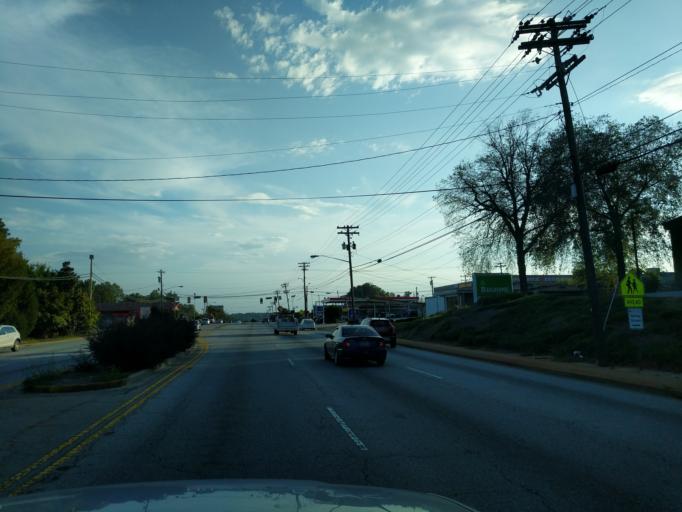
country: US
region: South Carolina
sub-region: Greenville County
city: Greenville
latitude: 34.8370
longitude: -82.3665
